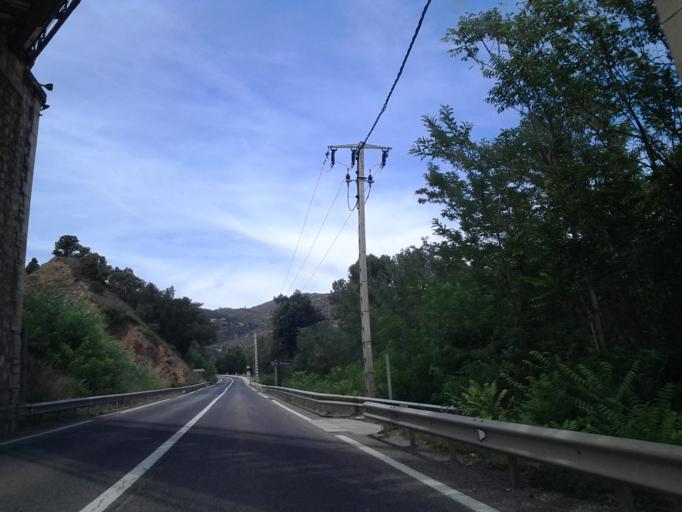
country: FR
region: Languedoc-Roussillon
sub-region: Departement des Pyrenees-Orientales
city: Vinca
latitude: 42.6494
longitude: 2.5562
